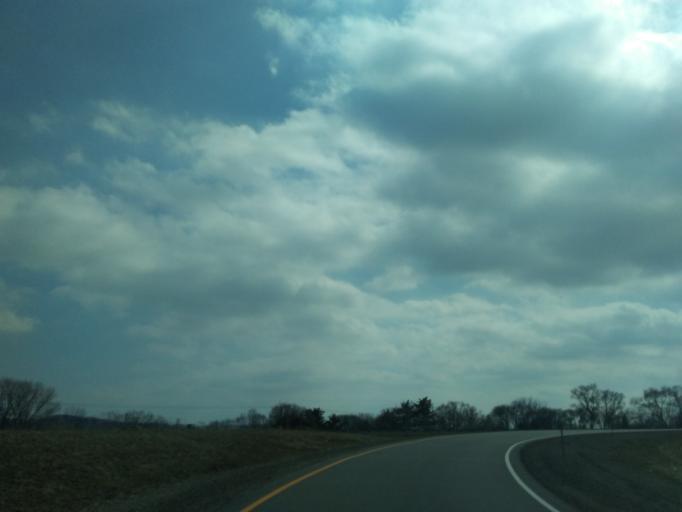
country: US
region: Wisconsin
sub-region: La Crosse County
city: Onalaska
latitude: 43.8664
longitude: -91.2331
